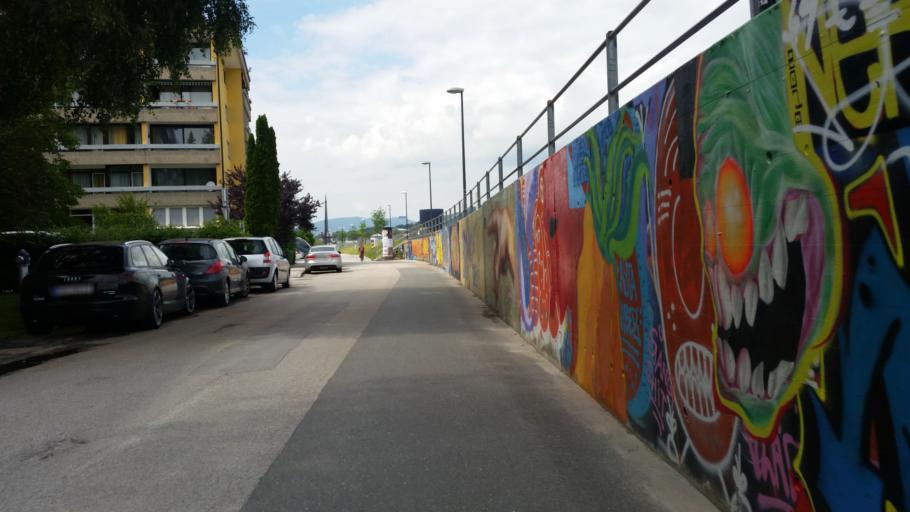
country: AT
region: Salzburg
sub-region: Politischer Bezirk Salzburg-Umgebung
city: Bergheim
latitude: 47.8186
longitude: 13.0347
